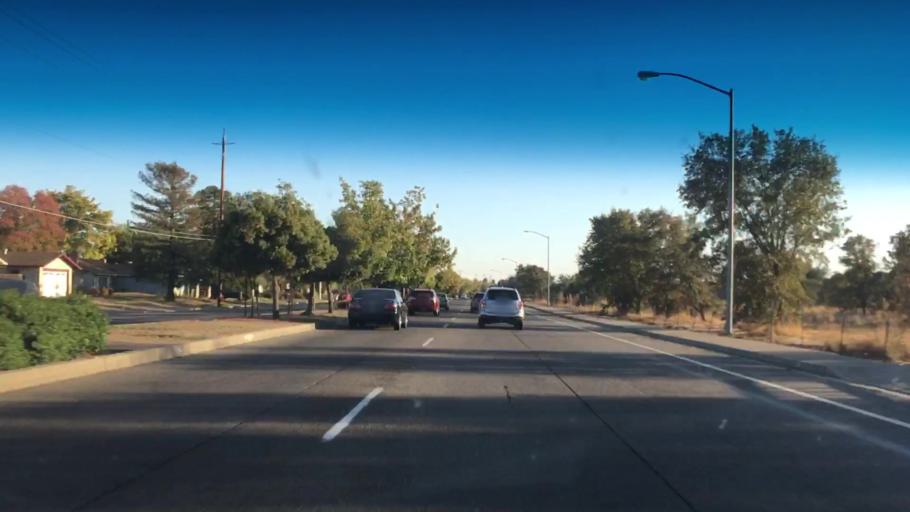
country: US
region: California
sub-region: Sacramento County
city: Laguna
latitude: 38.4552
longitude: -121.4456
